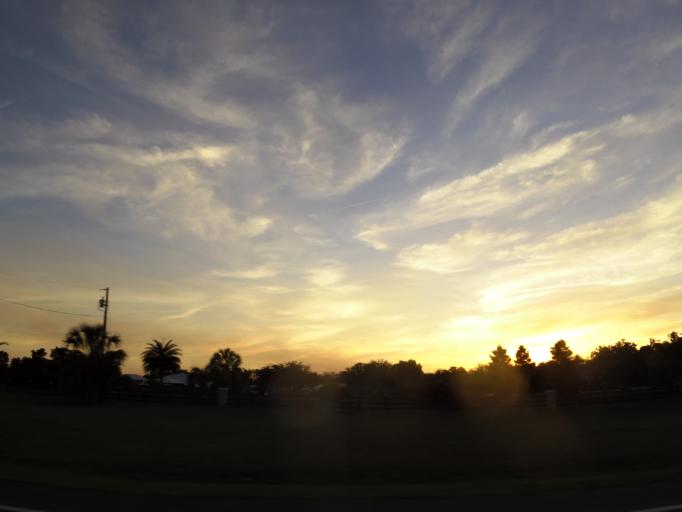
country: US
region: Florida
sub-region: Volusia County
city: De Leon Springs
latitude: 29.1464
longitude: -81.2875
